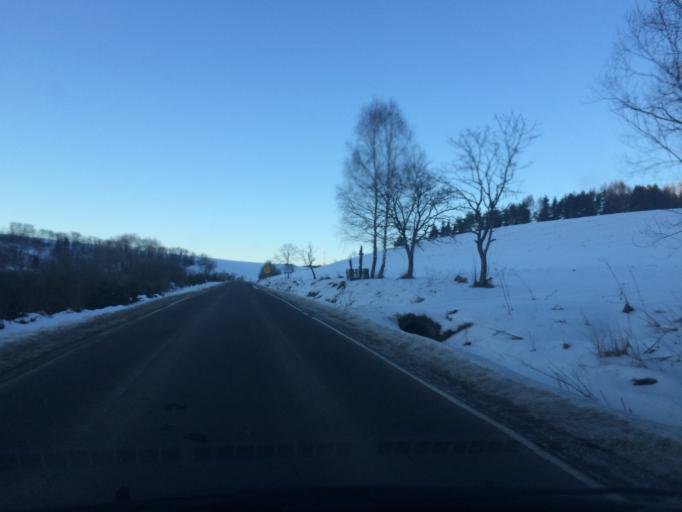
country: PL
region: Subcarpathian Voivodeship
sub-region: Powiat bieszczadzki
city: Lutowiska
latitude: 49.2349
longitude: 22.7003
